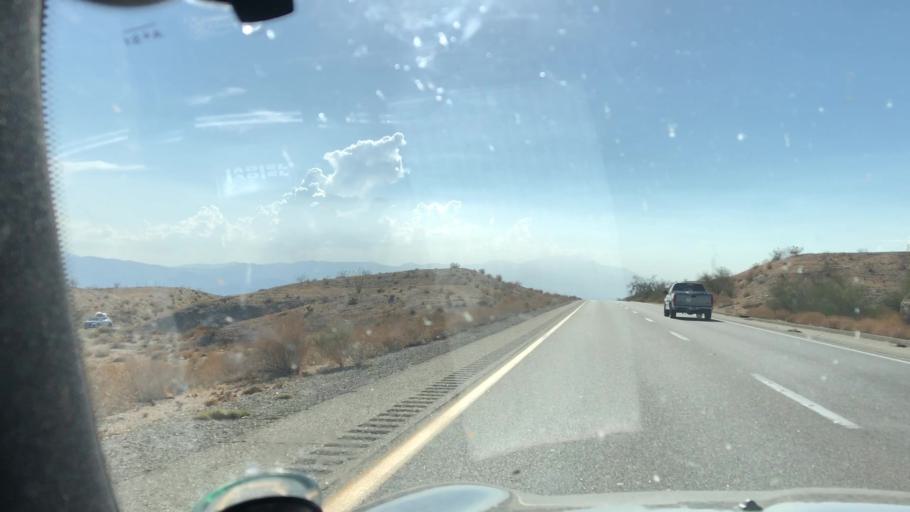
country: US
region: California
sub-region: Riverside County
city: Mecca
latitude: 33.6835
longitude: -116.0137
